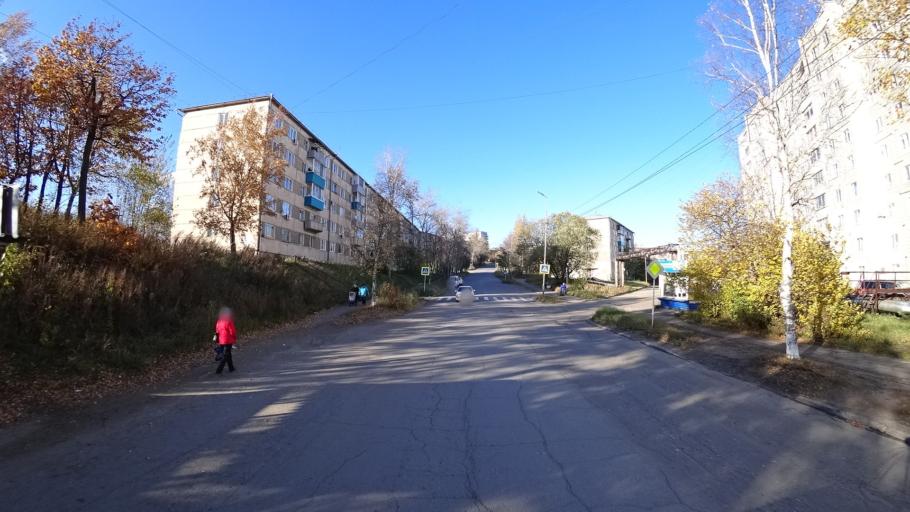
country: RU
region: Khabarovsk Krai
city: Amursk
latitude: 50.2380
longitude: 136.9049
